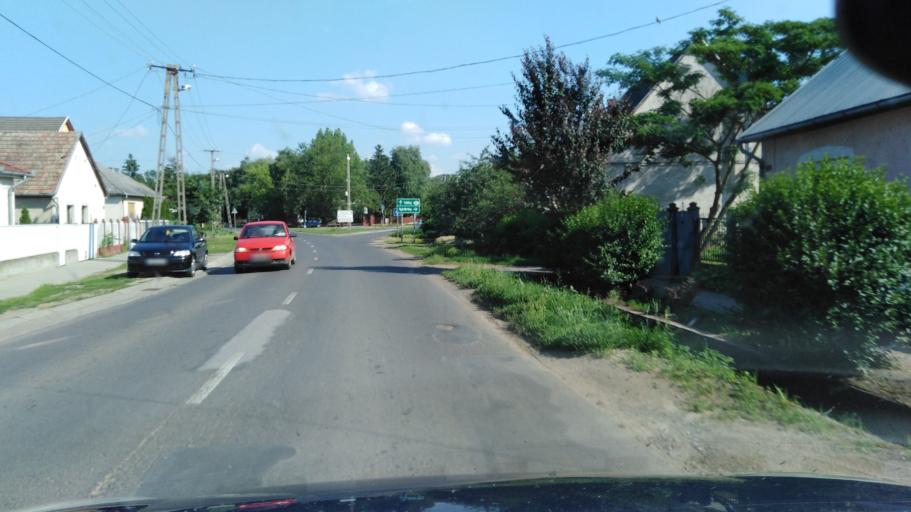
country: HU
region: Szabolcs-Szatmar-Bereg
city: Nyirbator
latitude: 47.8272
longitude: 22.1428
